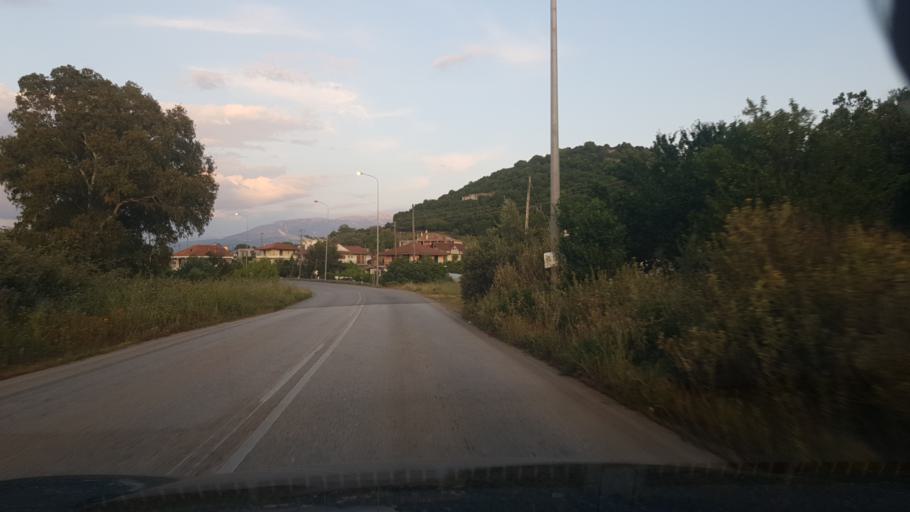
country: GR
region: Ionian Islands
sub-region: Lefkada
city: Lefkada
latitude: 38.8647
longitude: 20.7984
